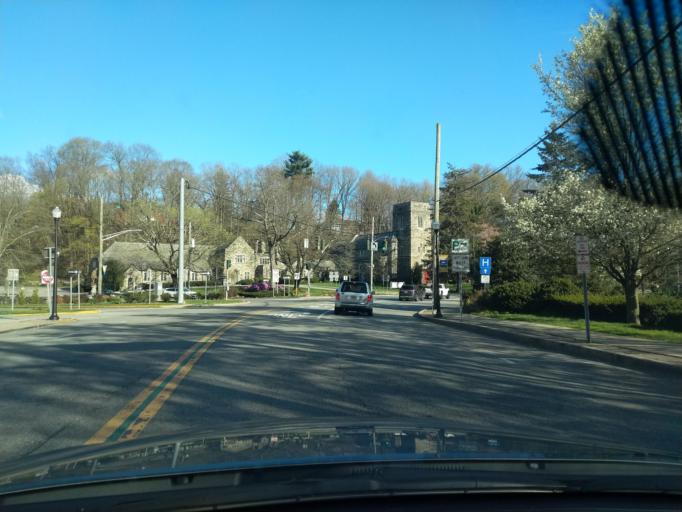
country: US
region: New York
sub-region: Westchester County
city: Mount Kisco
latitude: 41.2078
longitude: -73.7272
